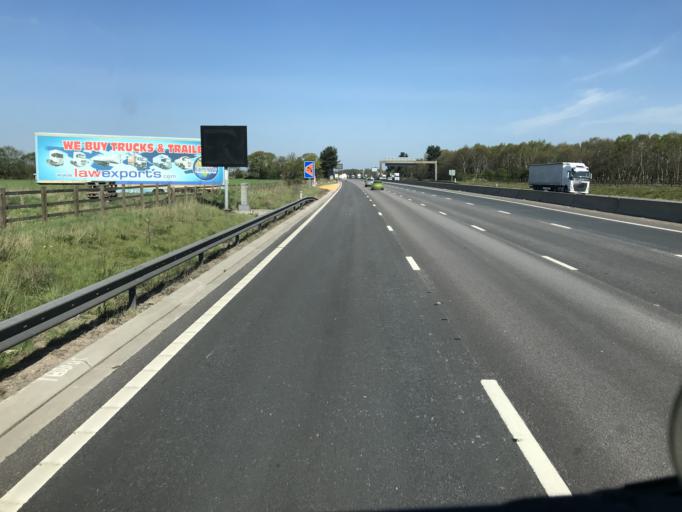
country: GB
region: England
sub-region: Cheshire East
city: Holmes Chapel
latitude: 53.2188
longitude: -2.3904
